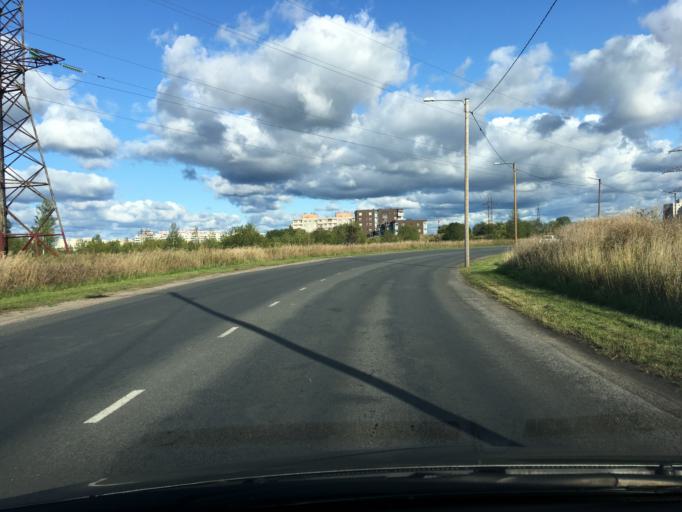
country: EE
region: Harju
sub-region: Tallinna linn
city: Kose
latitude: 59.4447
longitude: 24.8363
